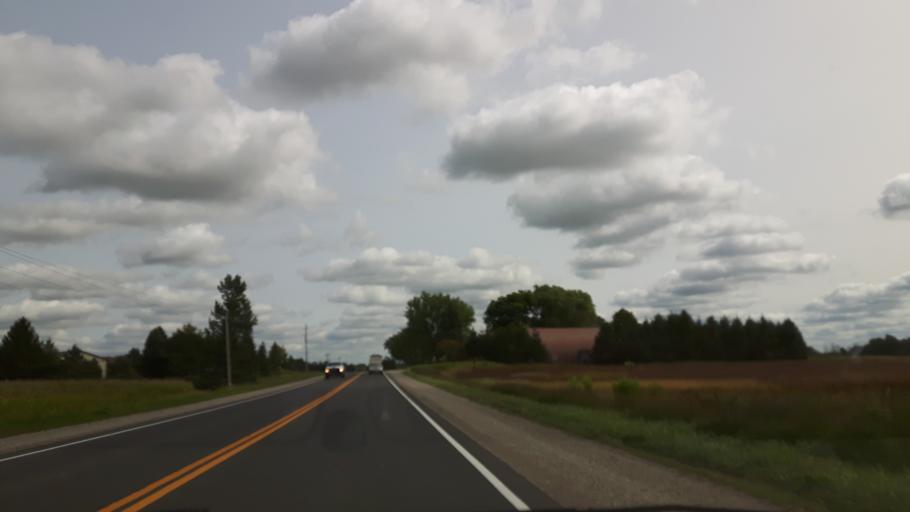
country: CA
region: Ontario
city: Huron East
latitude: 43.5686
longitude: -81.4281
